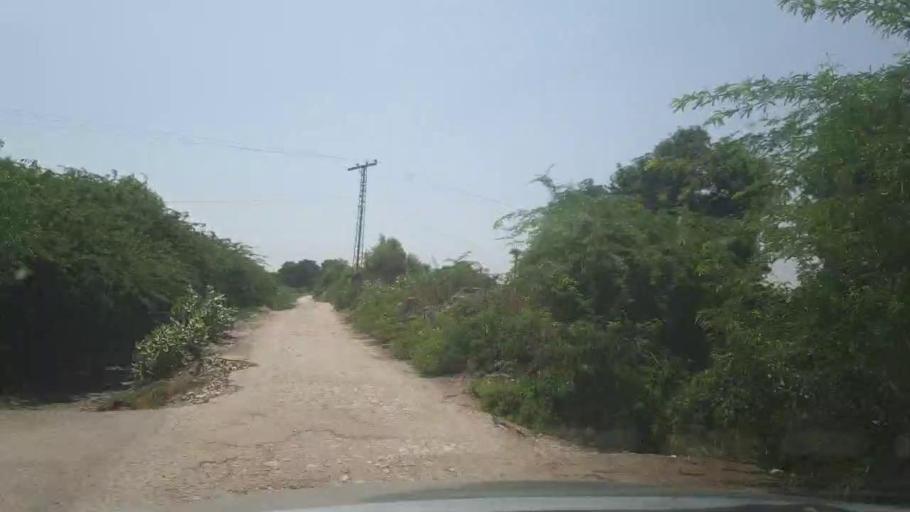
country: PK
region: Sindh
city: Khairpur
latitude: 27.3609
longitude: 69.0319
